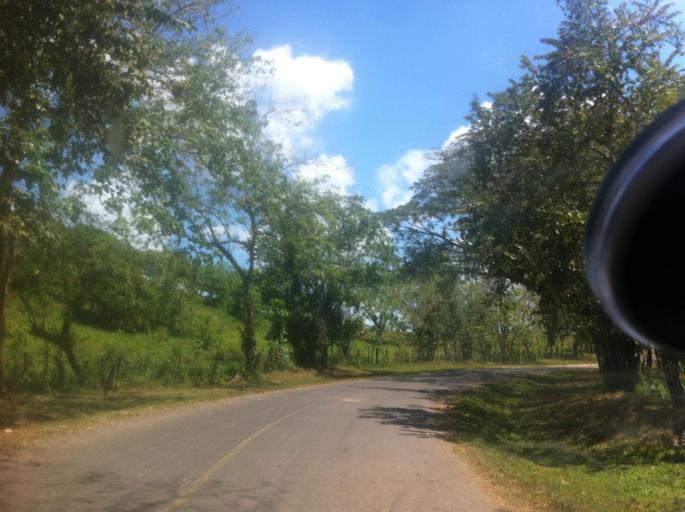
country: NI
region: Rio San Juan
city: San Carlos
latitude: 11.1423
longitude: -84.7619
